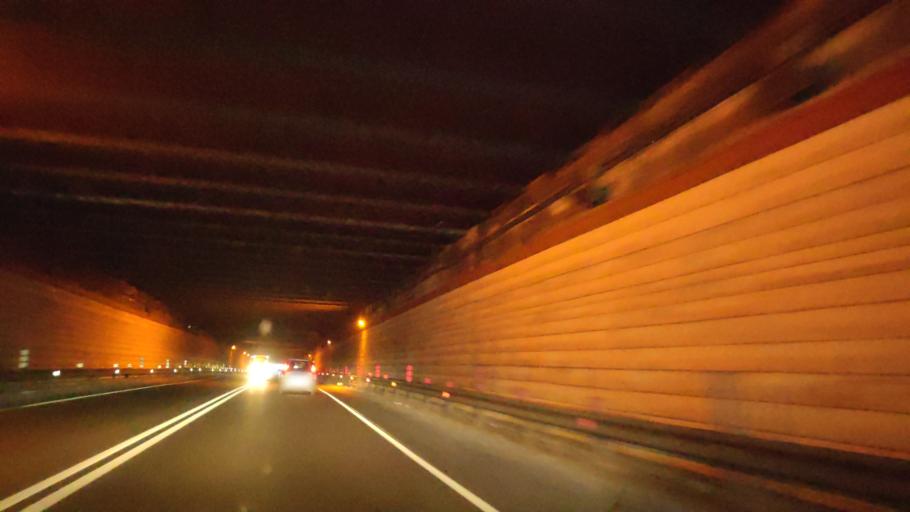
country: IT
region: Calabria
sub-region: Provincia di Catanzaro
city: Soverato Superiore
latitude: 38.6908
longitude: 16.5403
